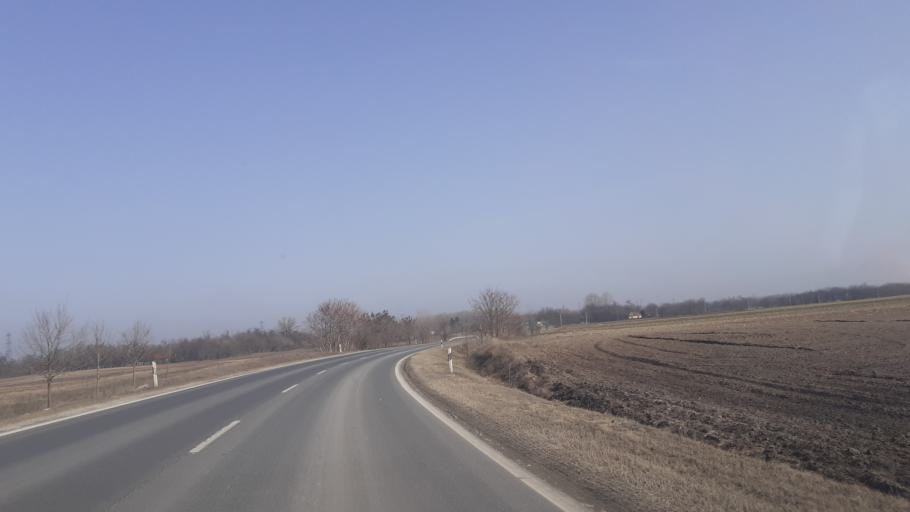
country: HU
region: Pest
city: Bugyi
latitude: 47.2408
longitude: 19.1226
